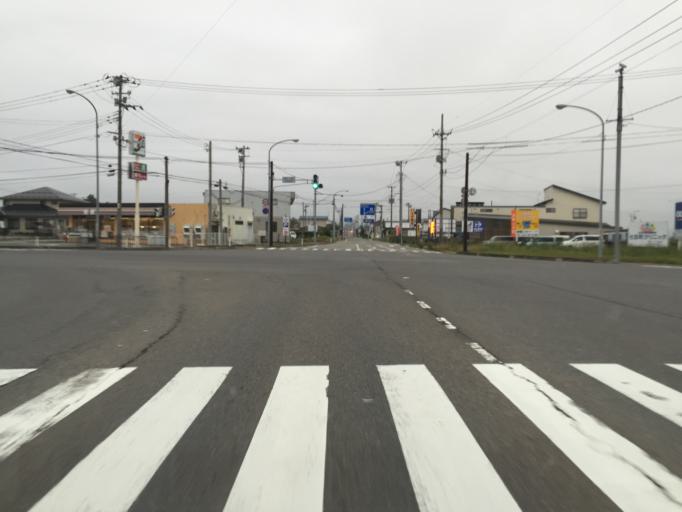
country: JP
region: Fukushima
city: Kitakata
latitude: 37.5158
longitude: 139.9023
